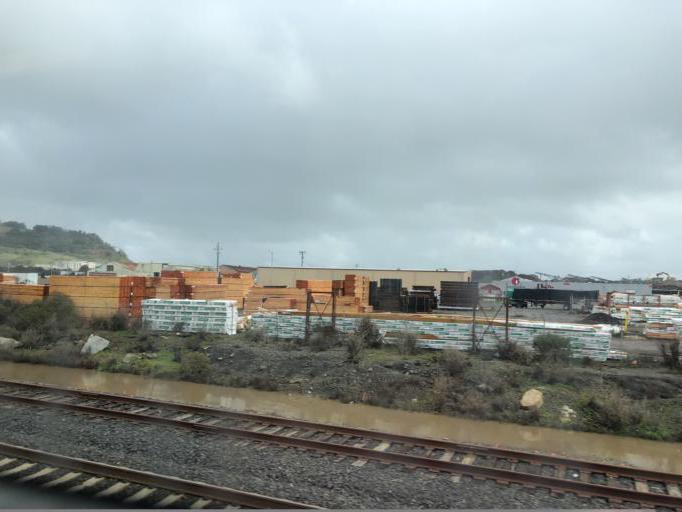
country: US
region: California
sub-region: San Mateo County
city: Brisbane
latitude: 37.7023
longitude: -122.4019
